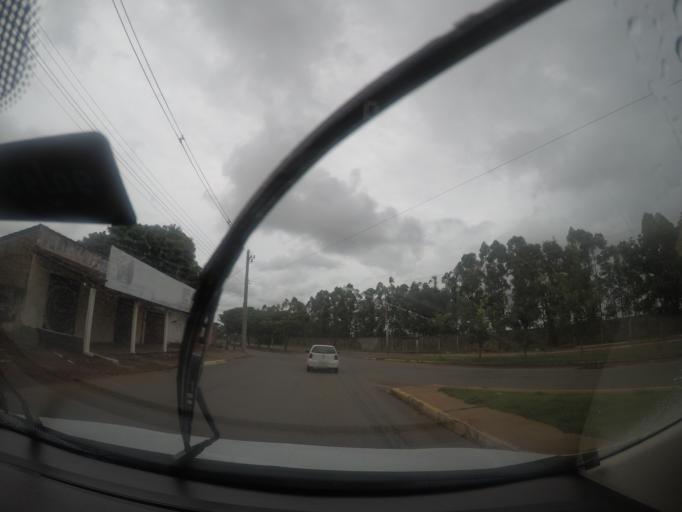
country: BR
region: Goias
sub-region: Trindade
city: Trindade
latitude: -16.6508
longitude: -49.3860
